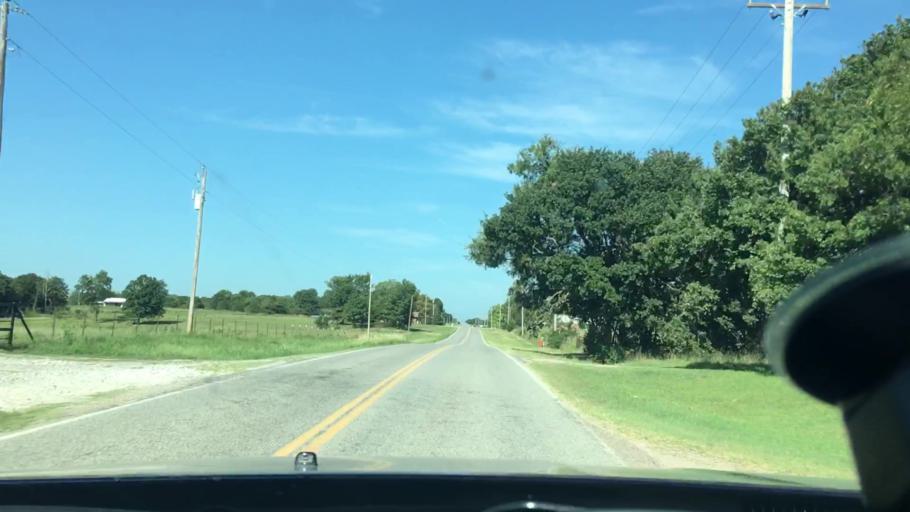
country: US
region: Oklahoma
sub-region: Johnston County
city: Tishomingo
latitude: 34.2741
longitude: -96.4923
